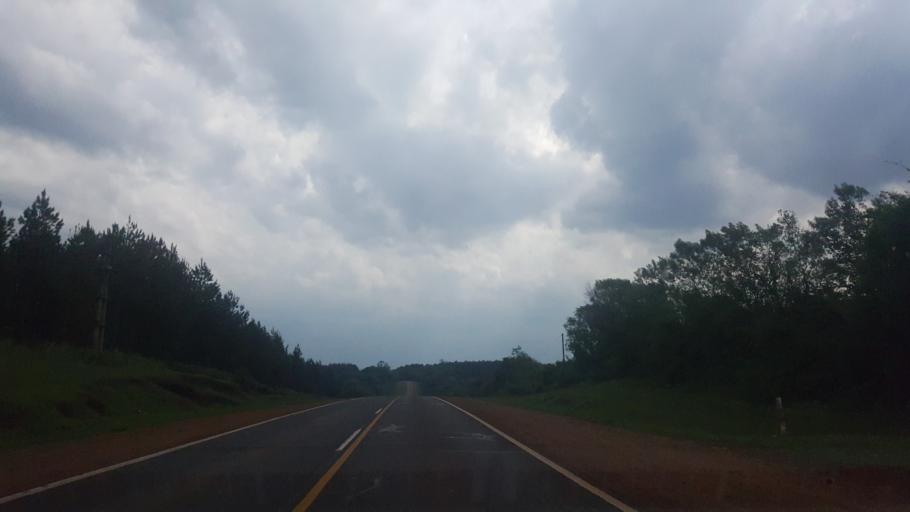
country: AR
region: Misiones
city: Santo Pipo
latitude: -27.1129
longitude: -55.3527
